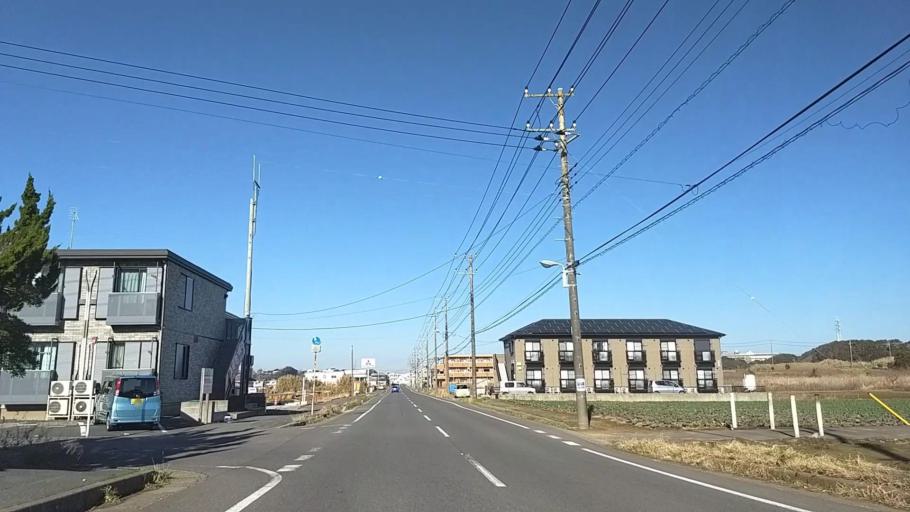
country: JP
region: Chiba
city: Hasaki
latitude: 35.7151
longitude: 140.8399
